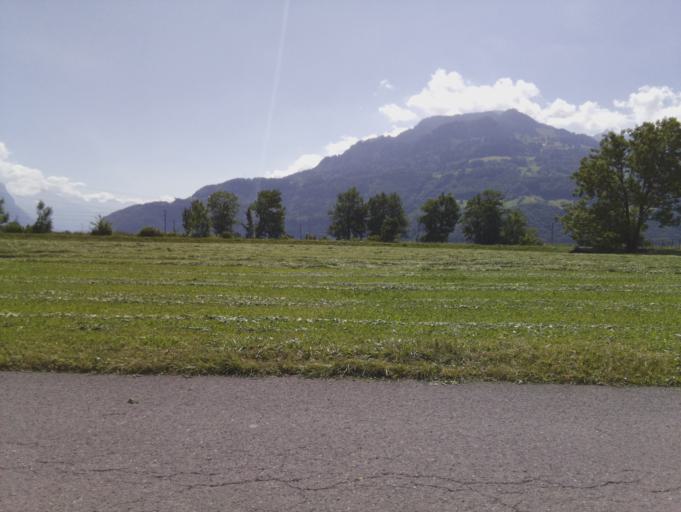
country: CH
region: Glarus
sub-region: Glarus
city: Niederurnen
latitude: 47.1285
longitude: 9.0606
